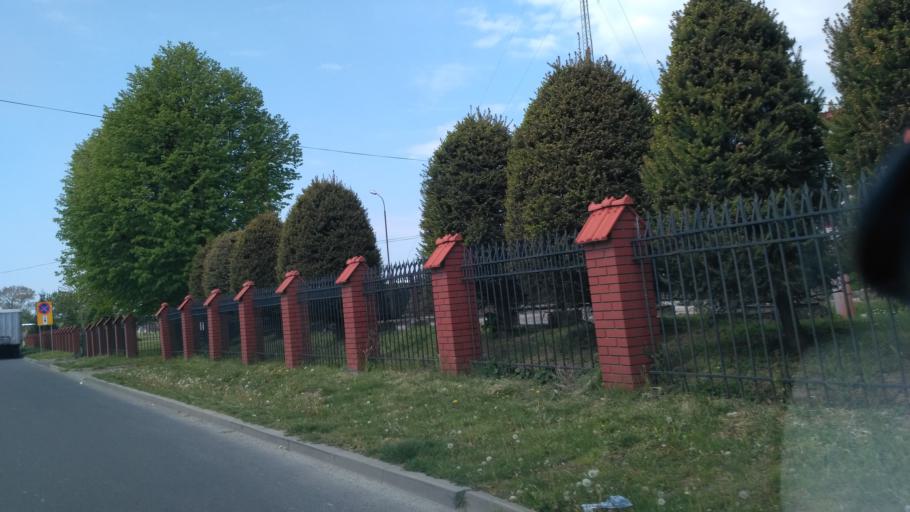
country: PL
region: Subcarpathian Voivodeship
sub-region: Powiat jaroslawski
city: Jaroslaw
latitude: 50.0029
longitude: 22.7108
